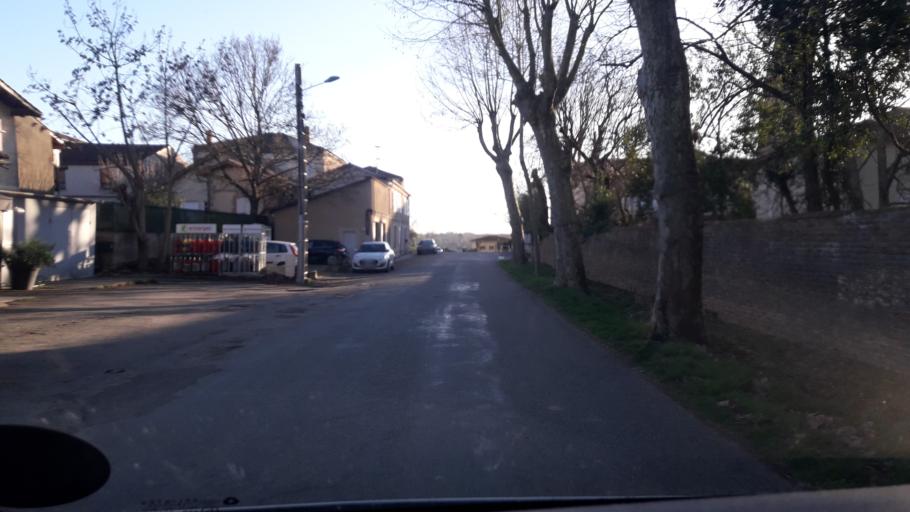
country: FR
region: Midi-Pyrenees
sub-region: Departement du Gers
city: Gimont
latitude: 43.5988
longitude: 0.9817
